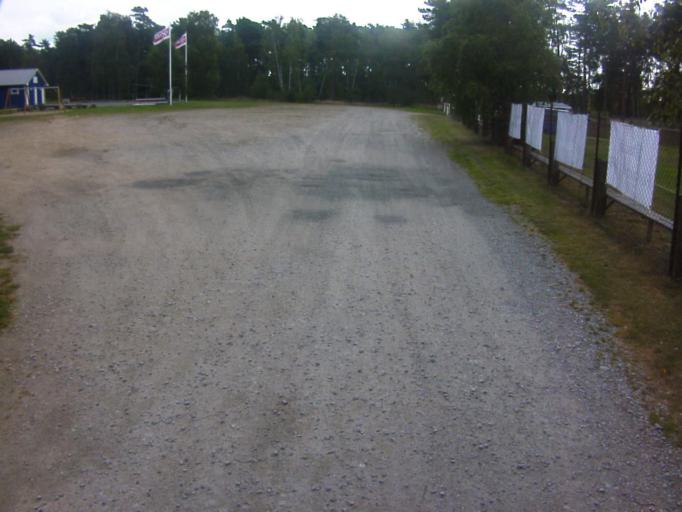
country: SE
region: Blekinge
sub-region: Karlshamns Kommun
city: Morrum
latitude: 56.0727
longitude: 14.7000
